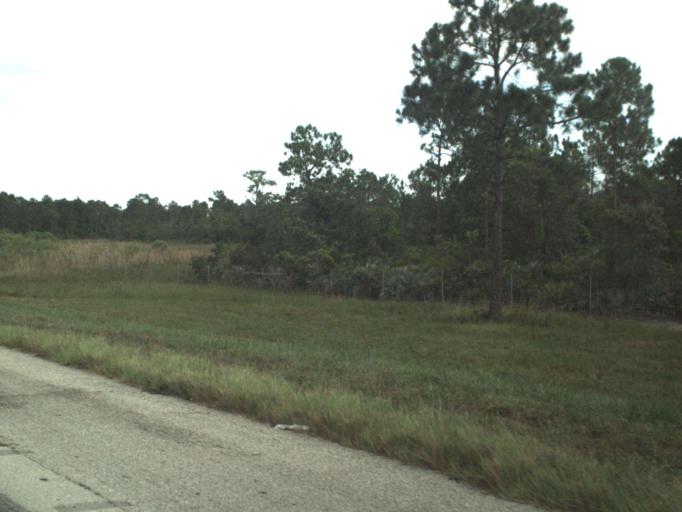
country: US
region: Florida
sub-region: Martin County
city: Palm City
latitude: 27.1413
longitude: -80.3692
